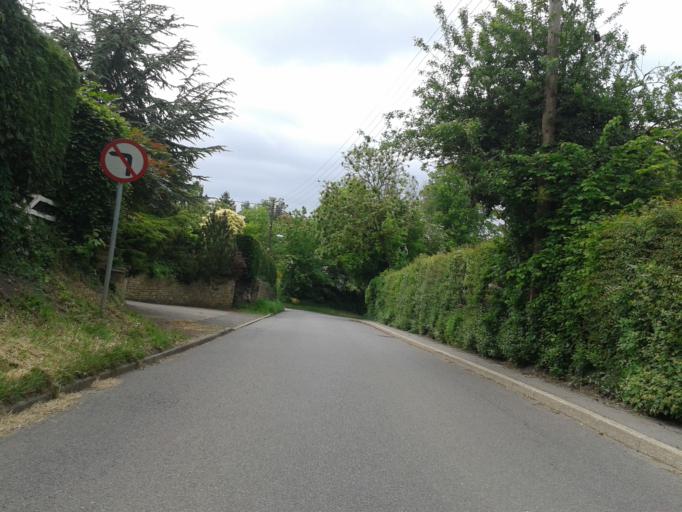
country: GB
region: England
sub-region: District of Rutland
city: Seaton
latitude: 52.5387
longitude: -0.6786
